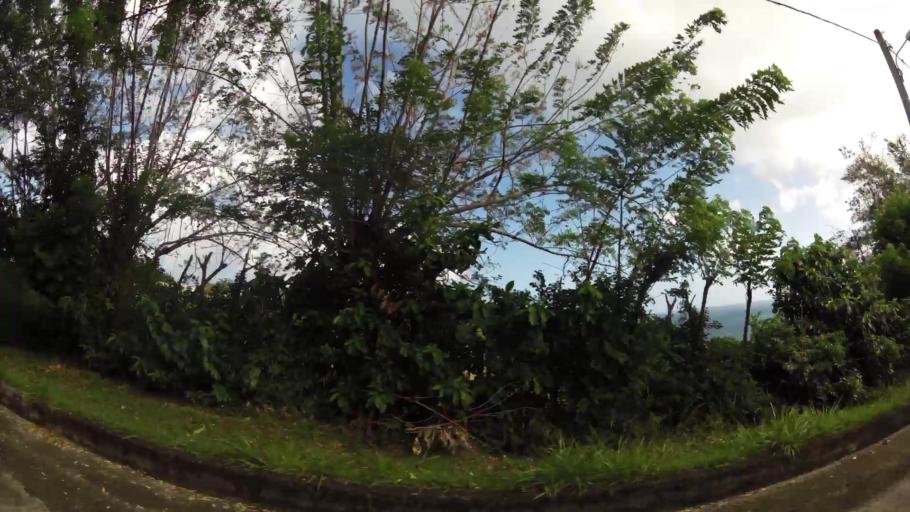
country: MQ
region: Martinique
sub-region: Martinique
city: Le Lorrain
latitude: 14.8158
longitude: -61.0242
